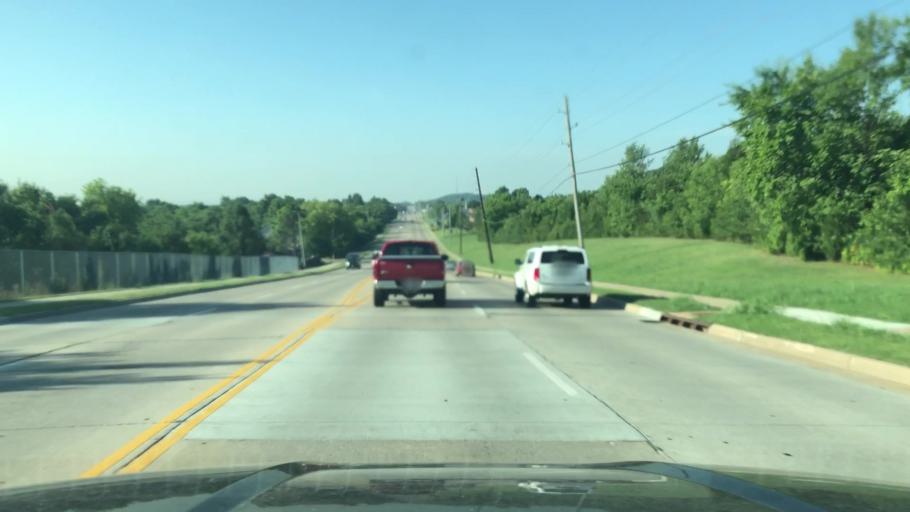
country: US
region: Oklahoma
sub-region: Tulsa County
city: Jenks
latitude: 36.0711
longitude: -95.9042
